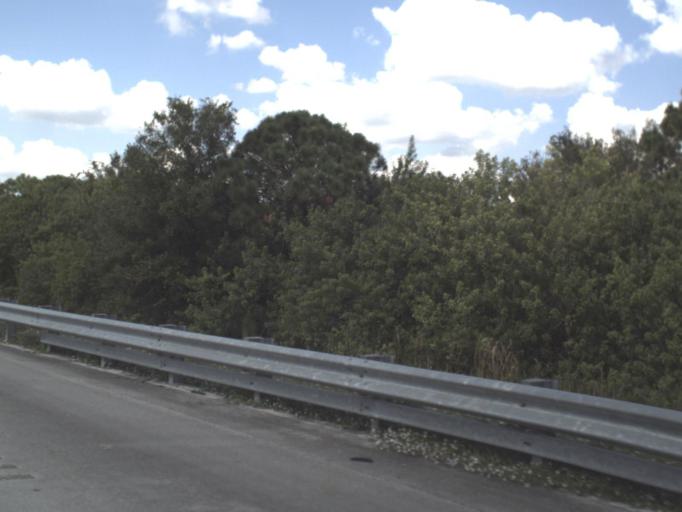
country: US
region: Florida
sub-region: Saint Lucie County
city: Lakewood Park
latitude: 27.4843
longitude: -80.4623
